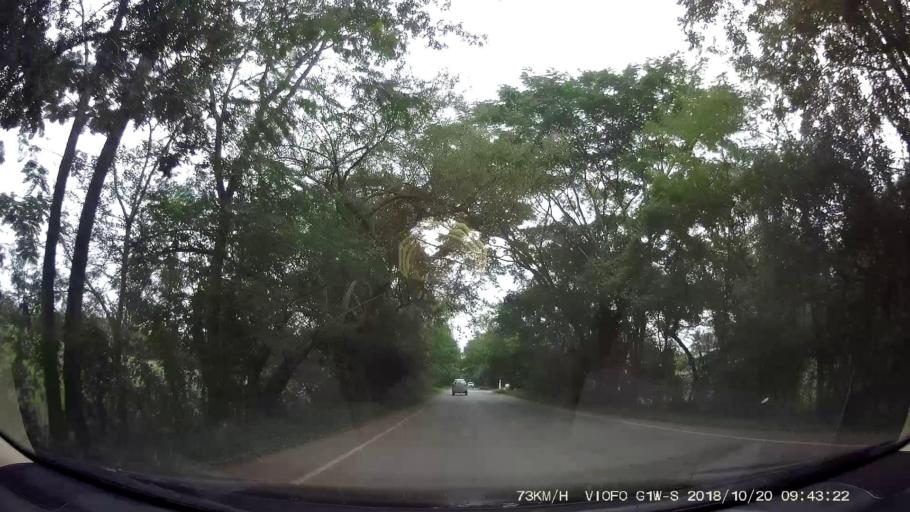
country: TH
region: Chaiyaphum
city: Khon San
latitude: 16.4729
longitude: 101.9484
